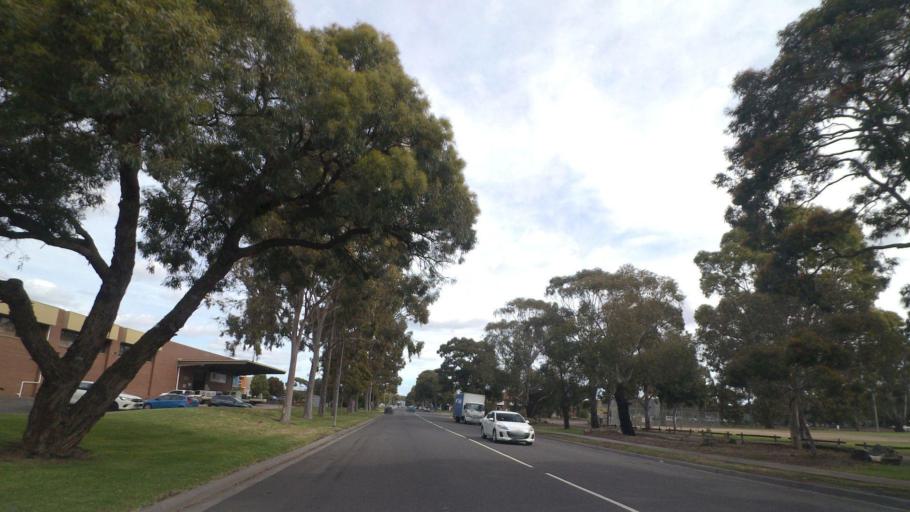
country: AU
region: Victoria
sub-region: Knox
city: Knoxfield
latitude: -37.8961
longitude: 145.2530
